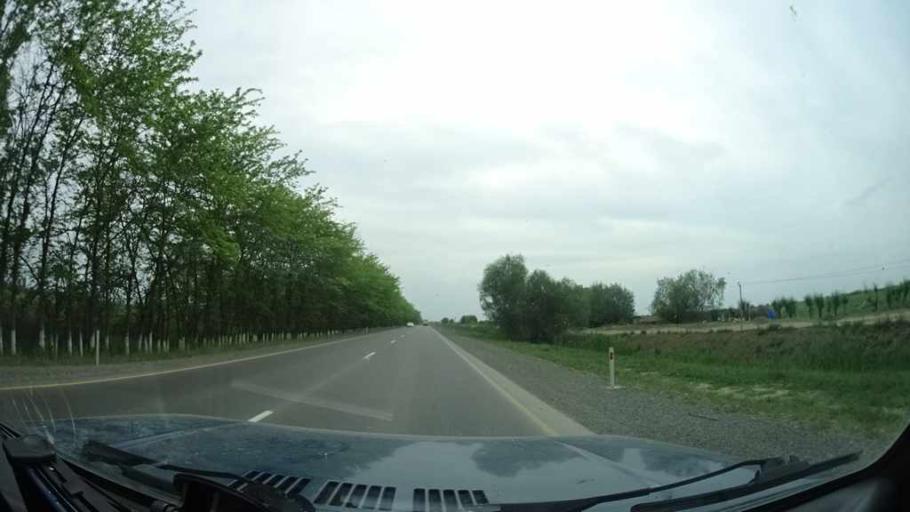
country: AZ
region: Aghjabadi Rayon
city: Agdzhabedy
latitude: 40.0373
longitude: 47.4004
